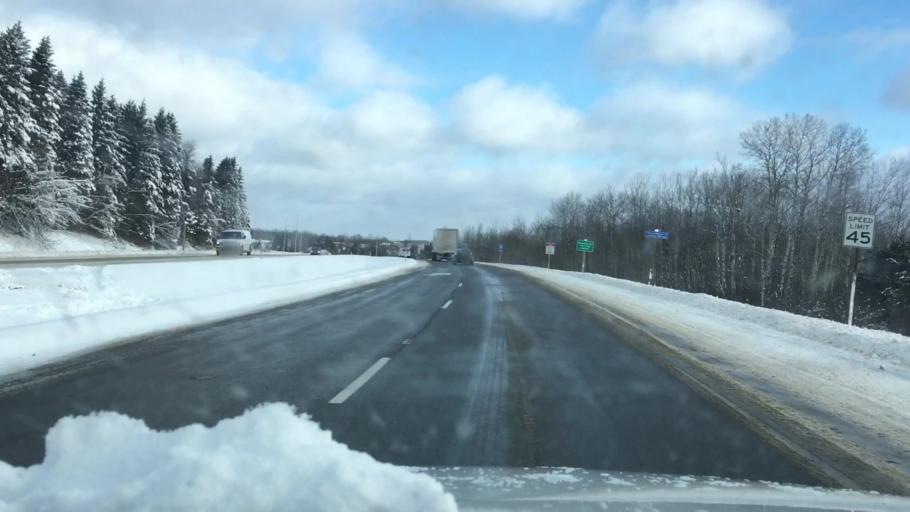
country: US
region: Maine
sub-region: Aroostook County
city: Caribou
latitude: 46.8647
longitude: -68.0000
